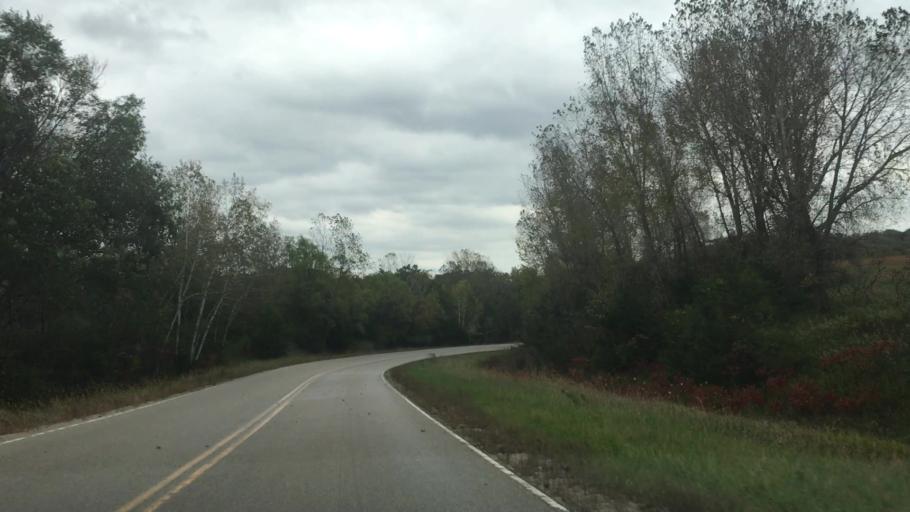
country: US
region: Minnesota
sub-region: Fillmore County
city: Preston
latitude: 43.7437
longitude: -92.0191
